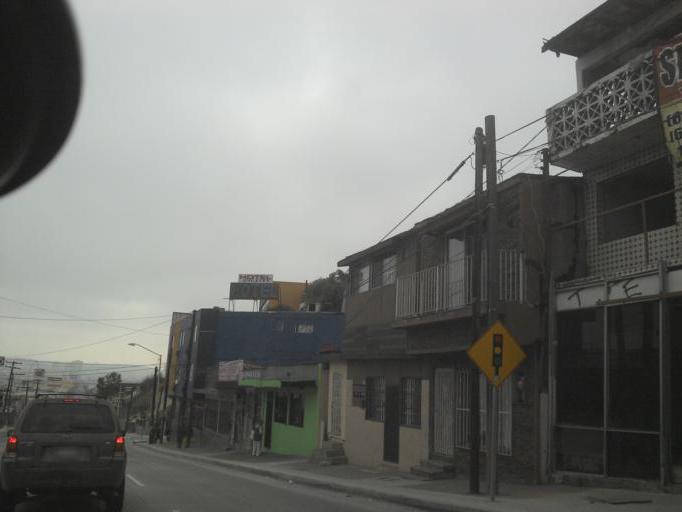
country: MX
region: Baja California
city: Tijuana
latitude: 32.5338
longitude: -117.0550
